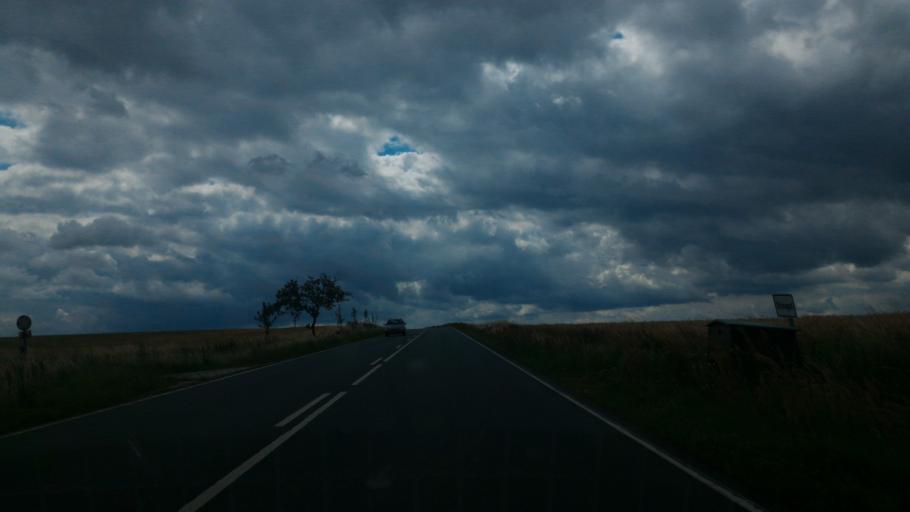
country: DE
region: Saxony
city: Goerlitz
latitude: 51.2001
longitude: 14.9439
